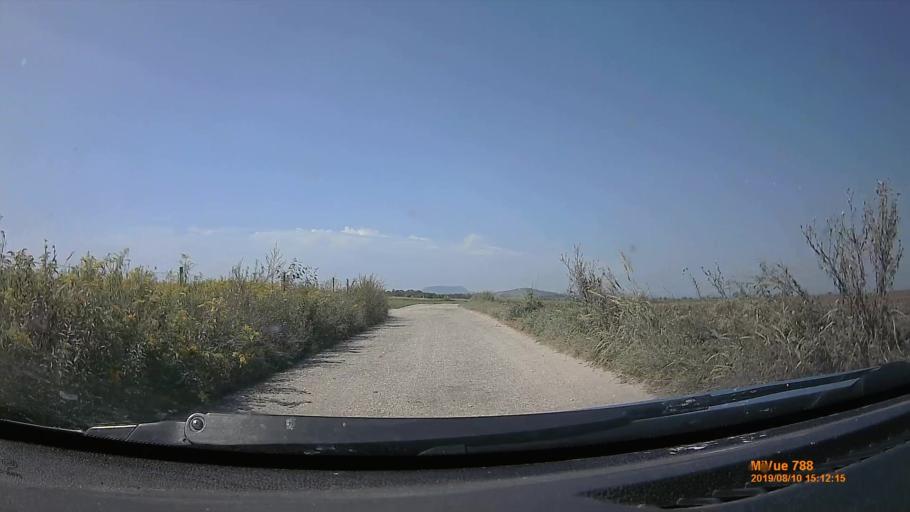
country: HU
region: Somogy
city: Fonyod
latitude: 46.6866
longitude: 17.5639
